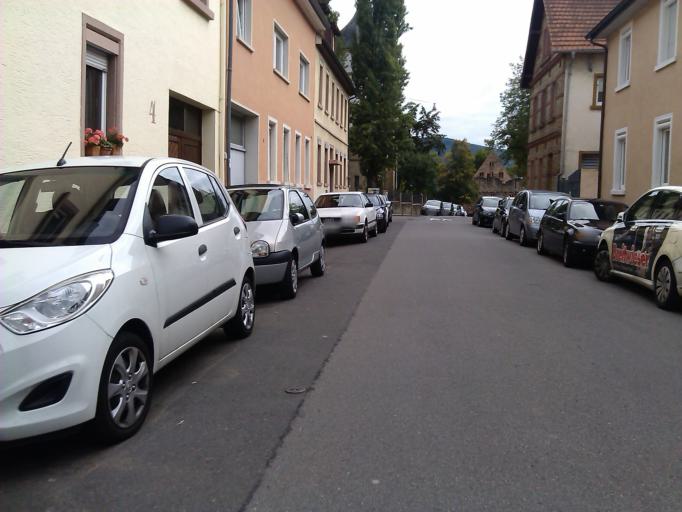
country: DE
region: Baden-Wuerttemberg
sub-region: Karlsruhe Region
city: Heidelberg
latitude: 49.4296
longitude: 8.6856
